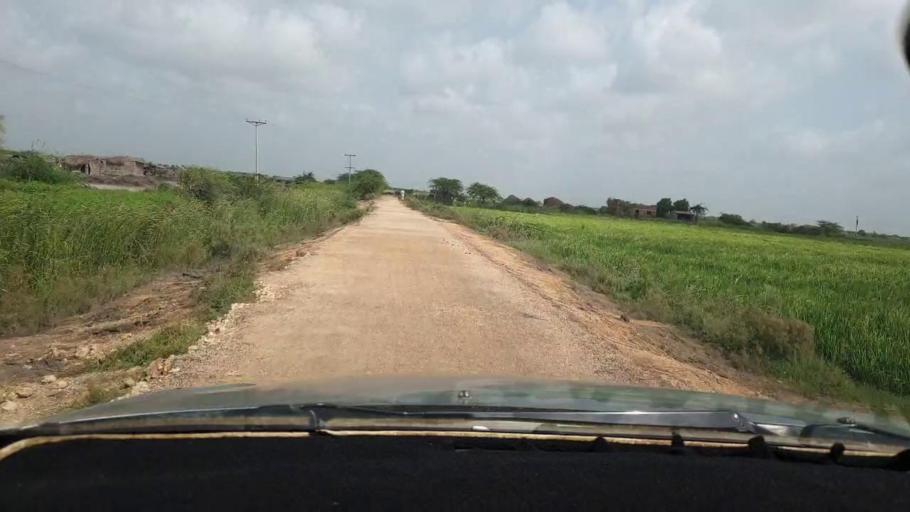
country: PK
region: Sindh
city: Tando Bago
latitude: 24.7553
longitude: 69.0966
